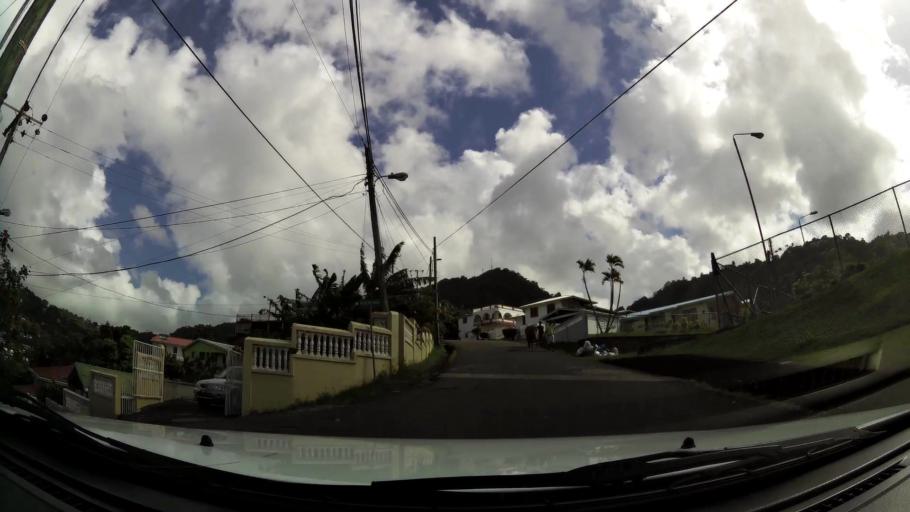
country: LC
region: Castries Quarter
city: Bisee
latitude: 14.0018
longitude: -60.9805
